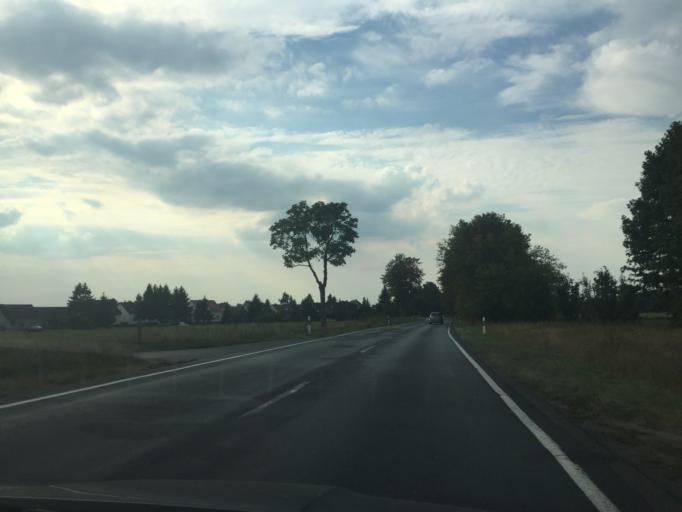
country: DE
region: Brandenburg
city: Spreenhagen
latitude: 52.3556
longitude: 13.8518
